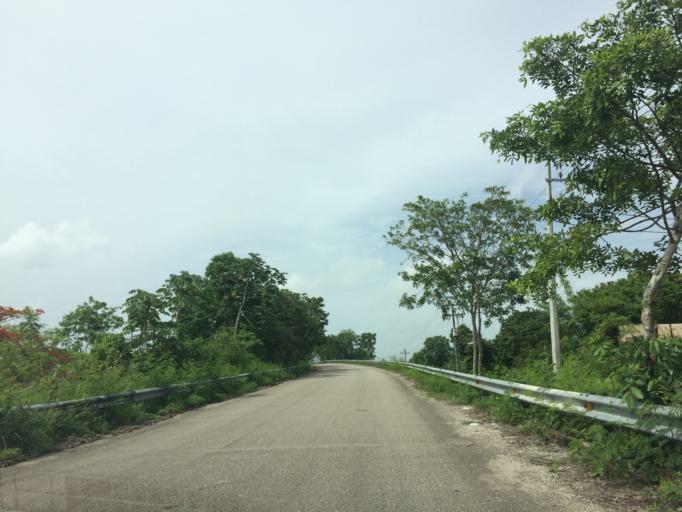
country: MX
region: Quintana Roo
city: Leona Vicario
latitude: 20.9430
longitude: -87.3224
